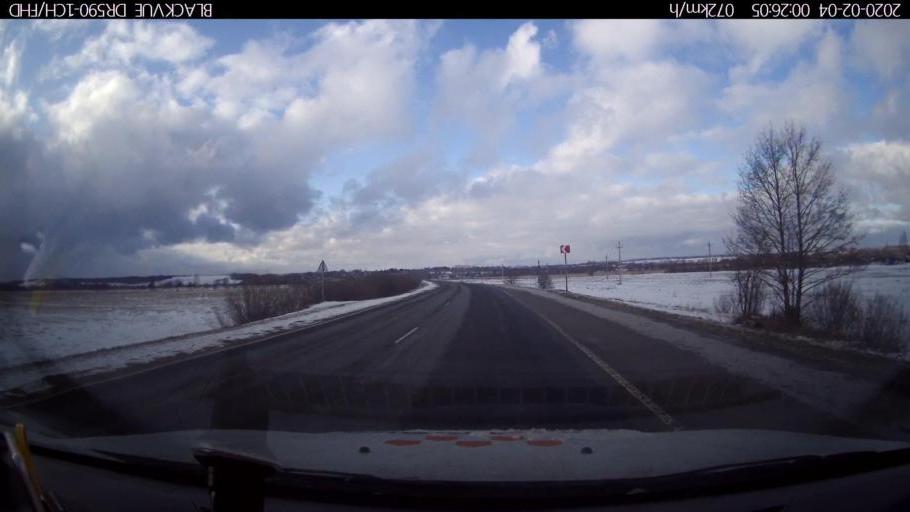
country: RU
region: Nizjnij Novgorod
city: Kstovo
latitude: 56.0115
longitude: 44.2040
